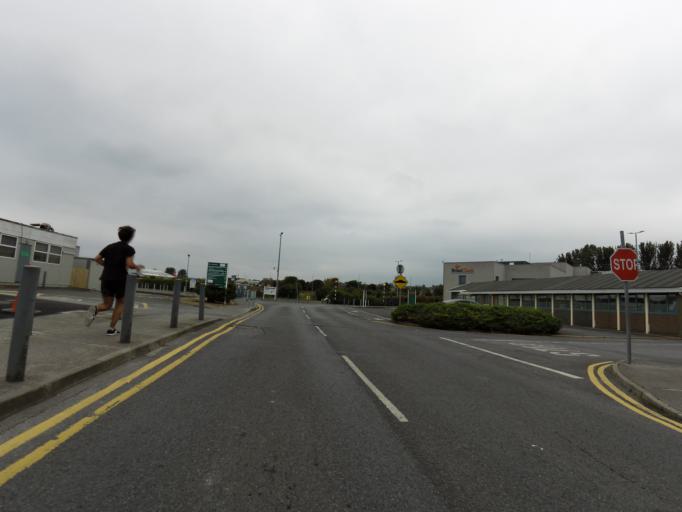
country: IE
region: Connaught
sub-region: County Galway
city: Gaillimh
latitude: 53.2780
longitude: -9.0675
